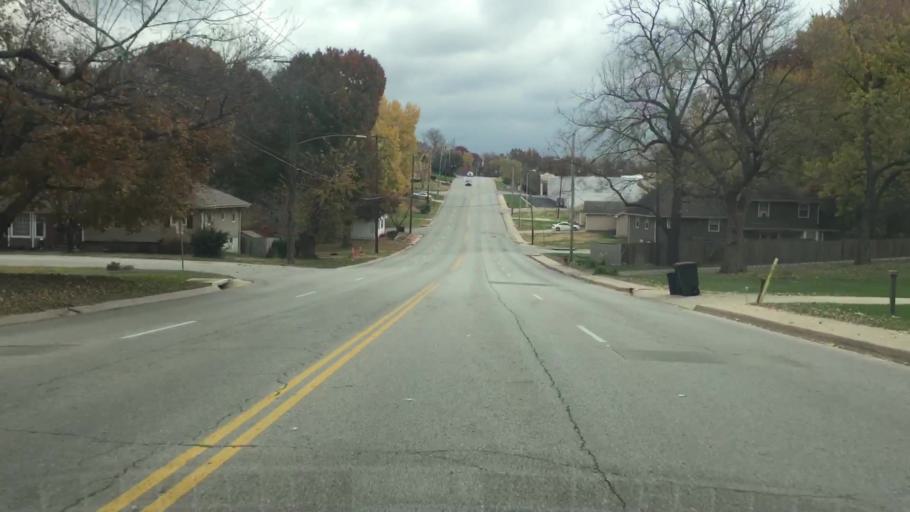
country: US
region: Missouri
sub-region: Jackson County
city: Raytown
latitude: 39.0082
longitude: -94.4493
